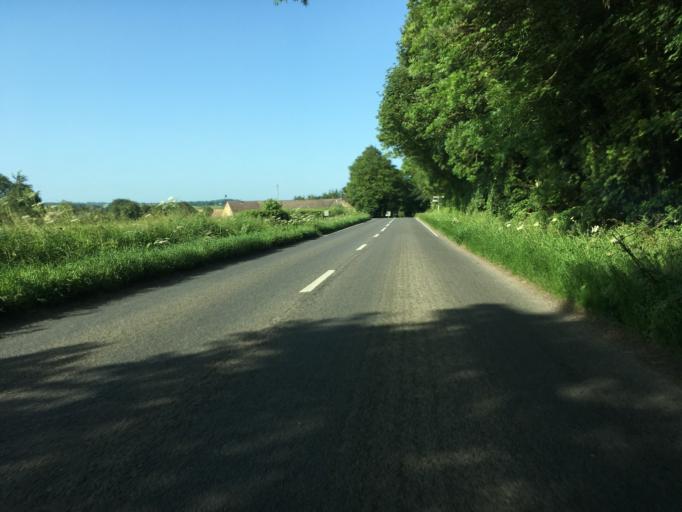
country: GB
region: England
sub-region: Oxfordshire
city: Charlbury
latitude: 51.9107
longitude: -1.4530
